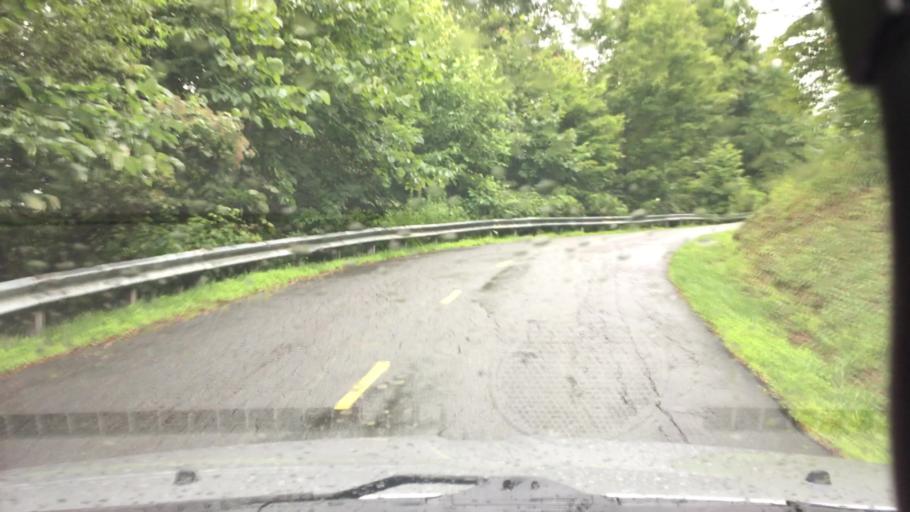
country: US
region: North Carolina
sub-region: Madison County
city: Mars Hill
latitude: 35.9431
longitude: -82.5146
